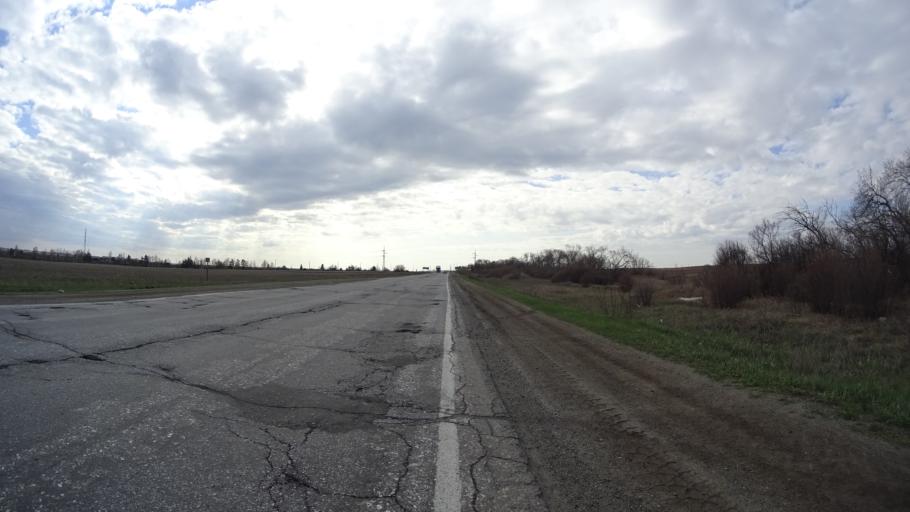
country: RU
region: Chelyabinsk
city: Troitsk
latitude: 54.0952
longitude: 61.4774
